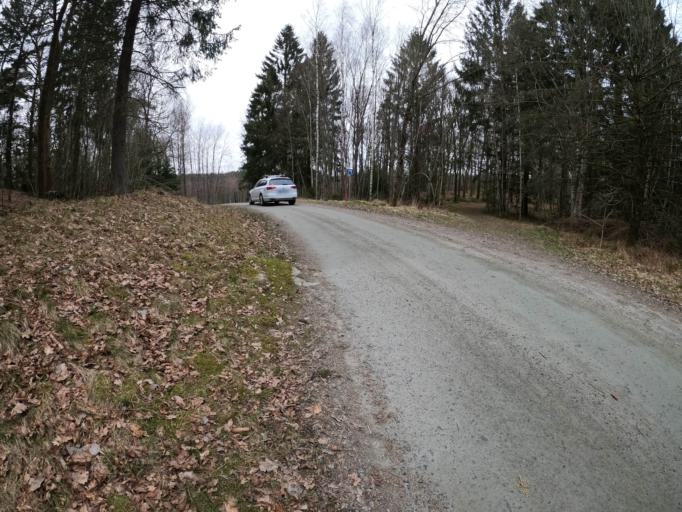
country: SE
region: Vaestra Goetaland
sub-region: Harryda Kommun
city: Molnlycke
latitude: 57.6318
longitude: 12.1044
